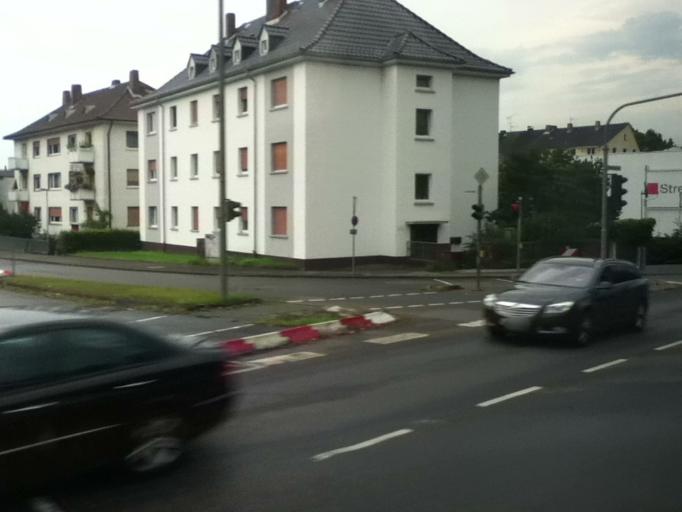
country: DE
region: Hesse
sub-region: Regierungsbezirk Giessen
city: Giessen
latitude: 50.5855
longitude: 8.6648
